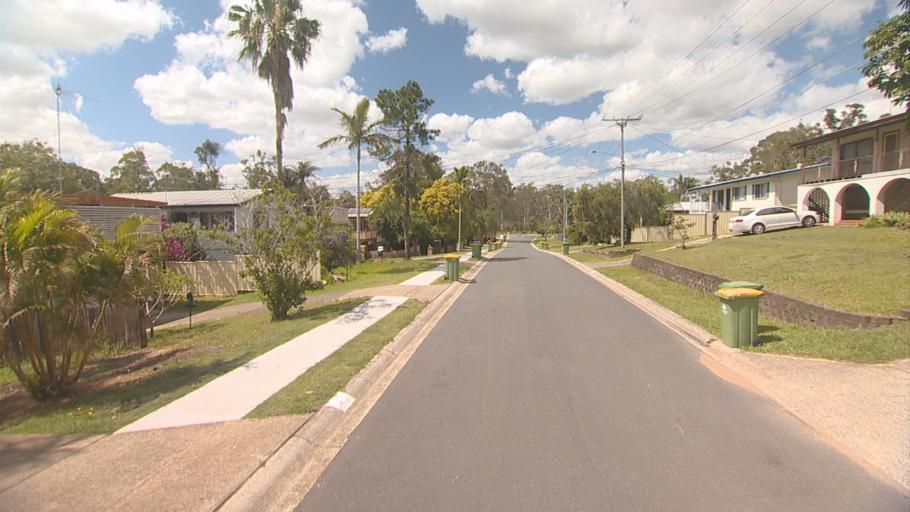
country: AU
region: Queensland
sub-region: Logan
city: Logan City
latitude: -27.6535
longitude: 153.1243
